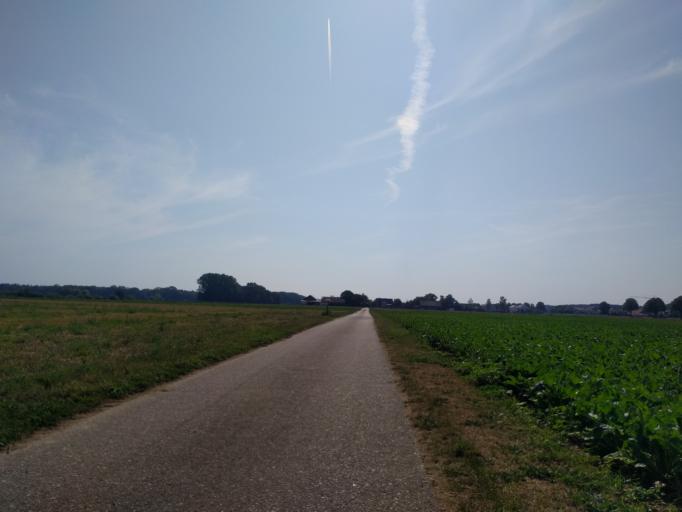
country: DE
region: Bavaria
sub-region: Upper Palatinate
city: Mintraching
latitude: 48.9897
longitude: 12.2498
